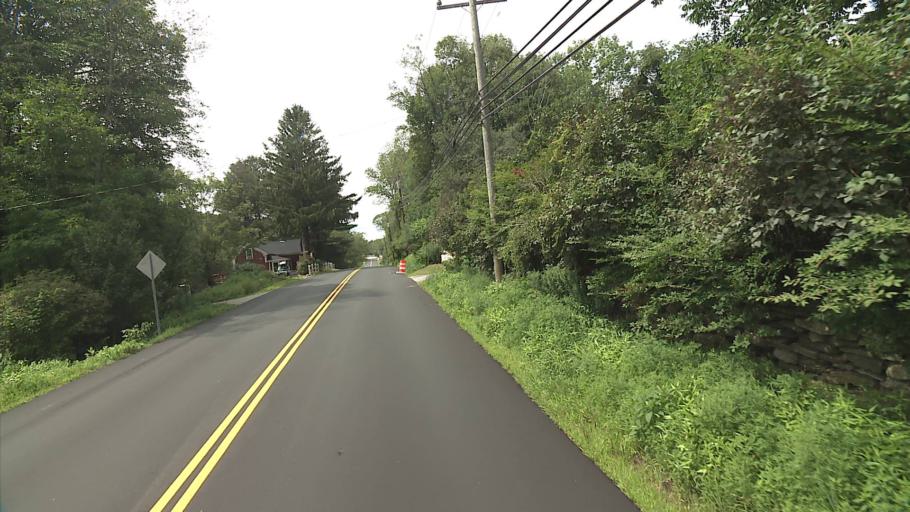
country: US
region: Connecticut
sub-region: Windham County
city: South Woodstock
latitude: 41.9534
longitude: -72.0364
